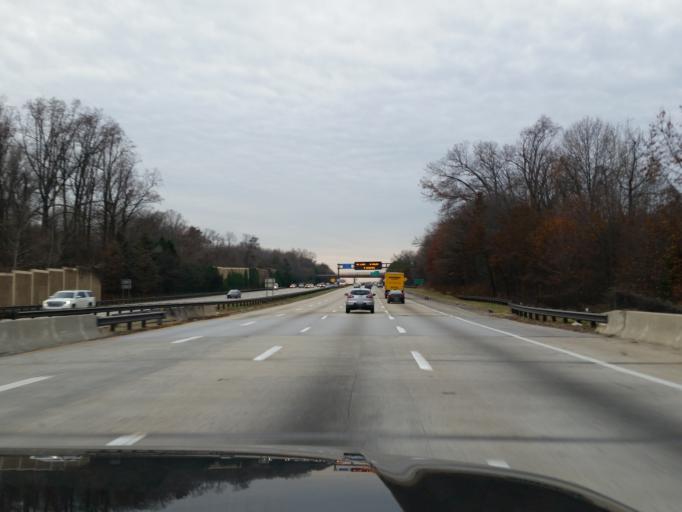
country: US
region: Maryland
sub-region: Prince George's County
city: Springdale
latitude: 38.9469
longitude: -76.8184
